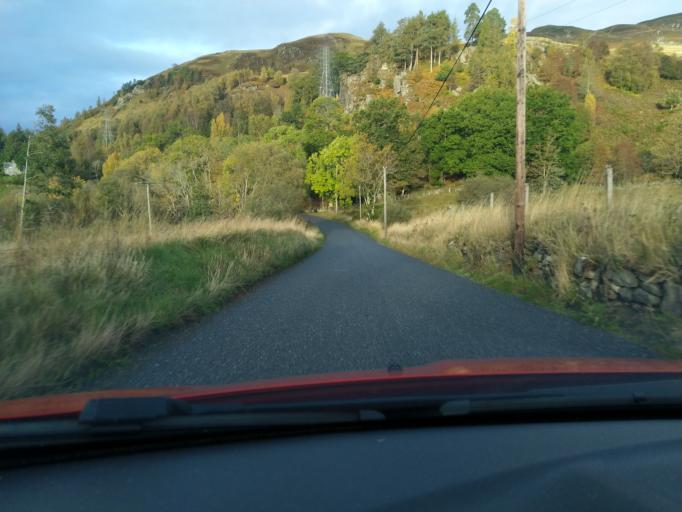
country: GB
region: Scotland
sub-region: Perth and Kinross
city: Aberfeldy
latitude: 56.7038
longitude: -4.1302
